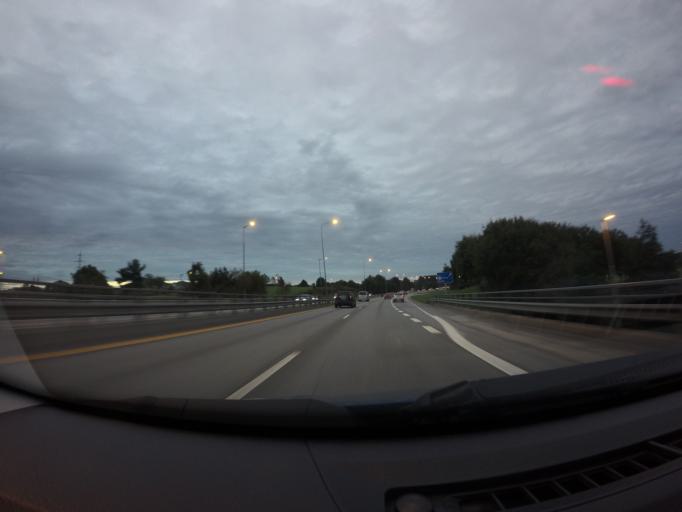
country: NO
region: Rogaland
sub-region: Stavanger
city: Stavanger
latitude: 58.9224
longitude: 5.7066
